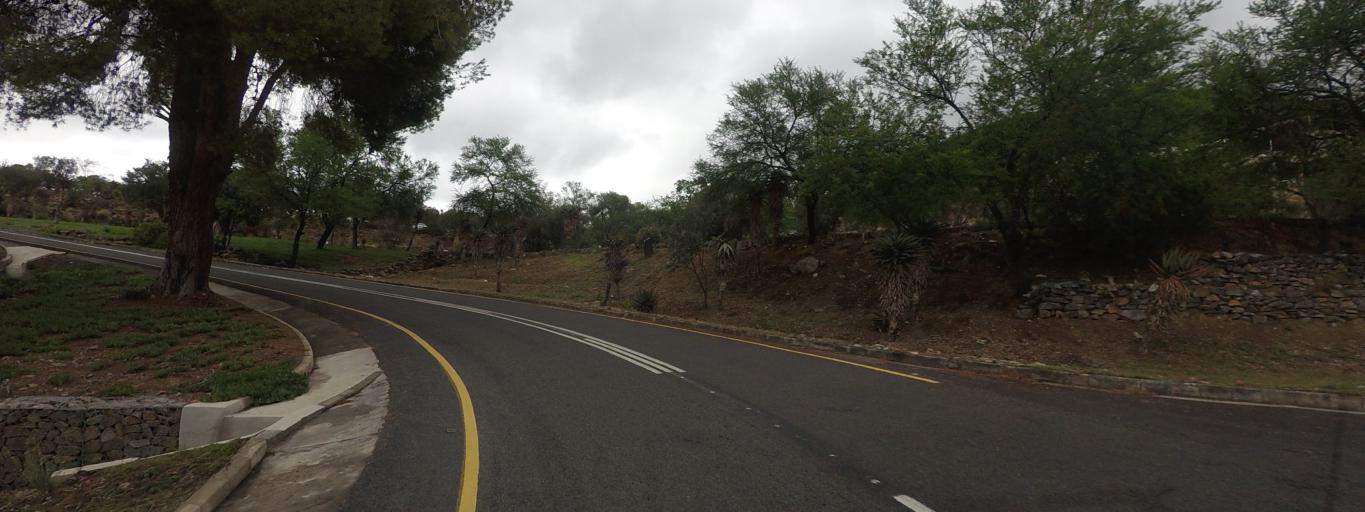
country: ZA
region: Western Cape
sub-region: Eden District Municipality
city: Oudtshoorn
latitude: -33.3932
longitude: 22.2156
